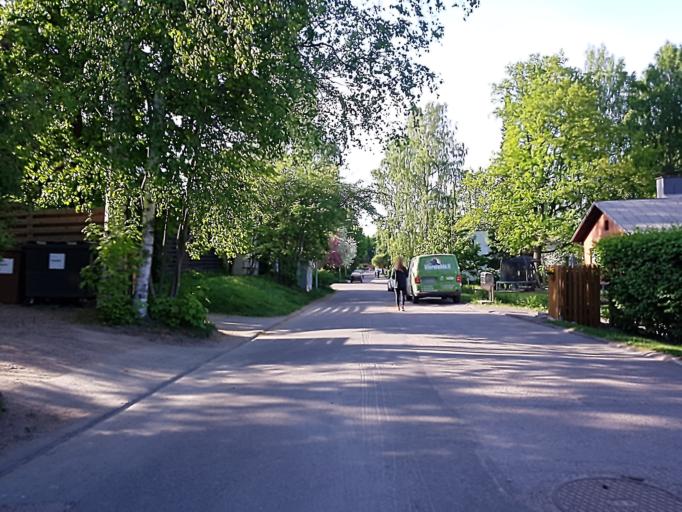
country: FI
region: Uusimaa
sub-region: Helsinki
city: Helsinki
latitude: 60.2450
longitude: 24.9398
